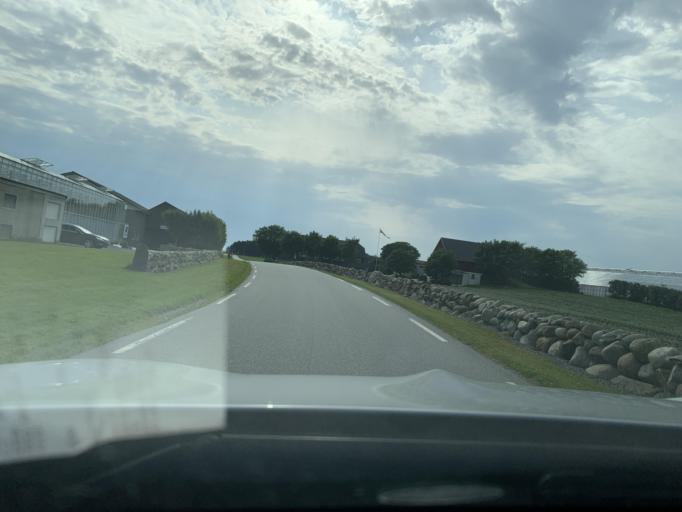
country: NO
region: Rogaland
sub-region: Klepp
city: Kleppe
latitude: 58.7176
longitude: 5.5430
